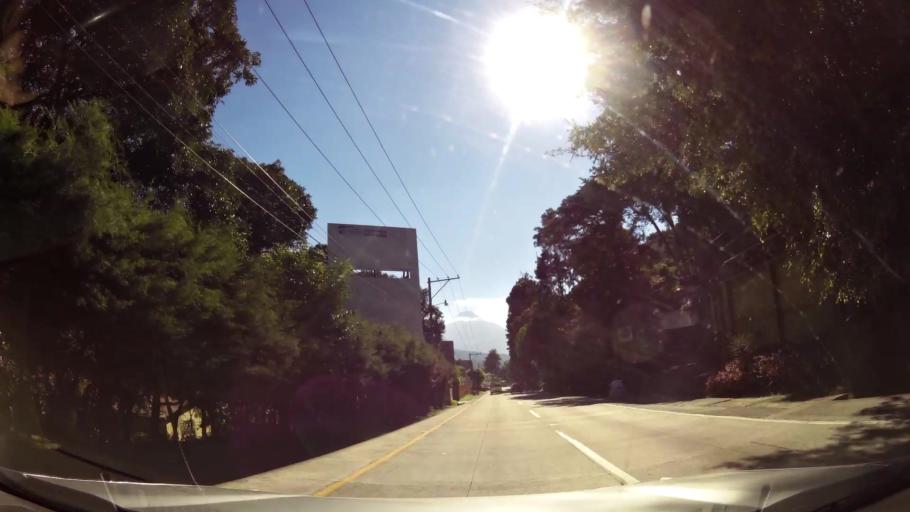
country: GT
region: Sacatepequez
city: Santa Lucia Milpas Altas
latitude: 14.5817
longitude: -90.6646
